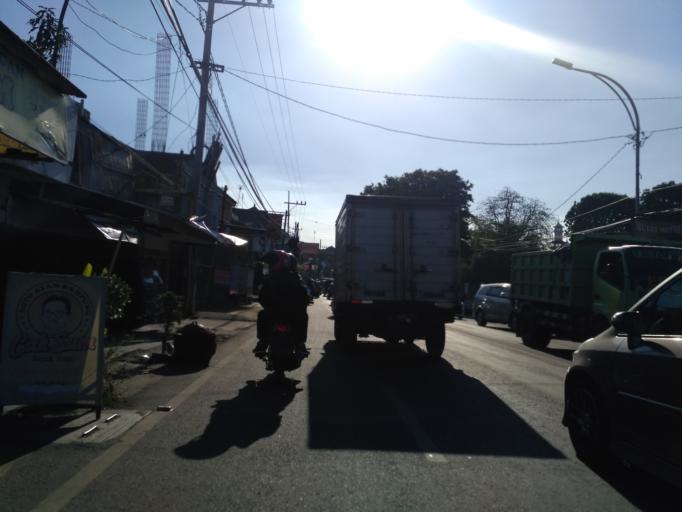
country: ID
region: East Java
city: Malang
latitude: -7.9236
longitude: 112.5980
